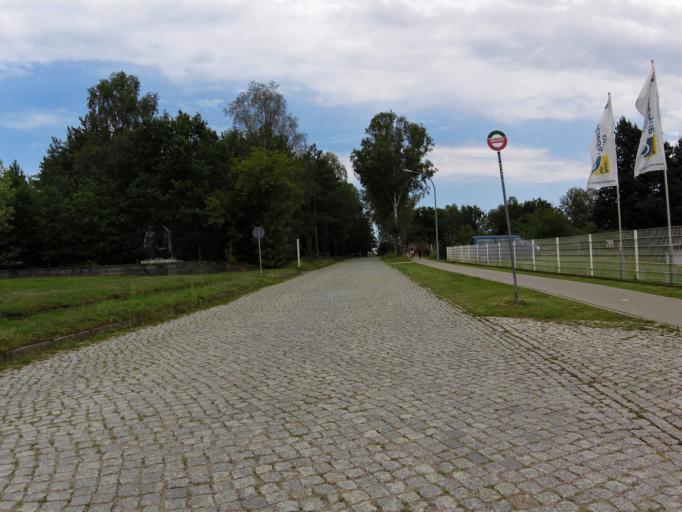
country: DE
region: Brandenburg
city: Furstenberg
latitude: 53.1947
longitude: 13.1501
